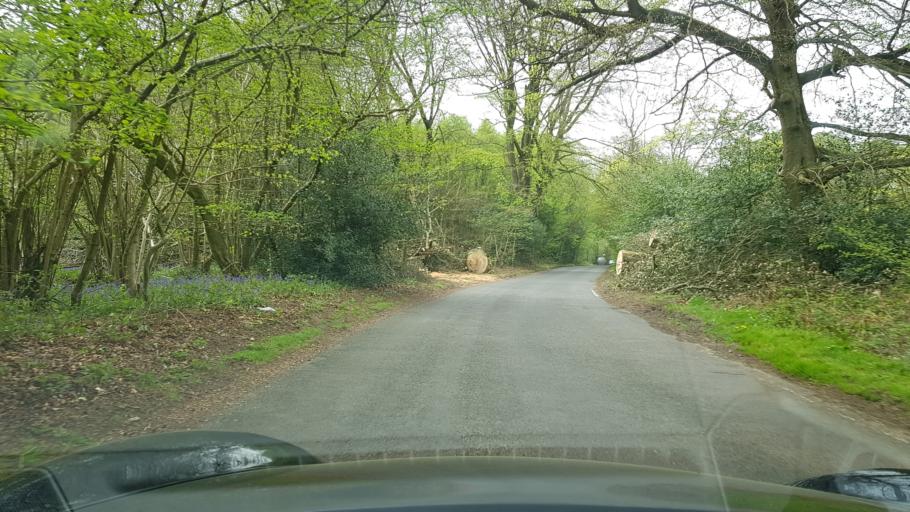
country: GB
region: England
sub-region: Surrey
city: East Horsley
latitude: 51.2344
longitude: -0.4608
